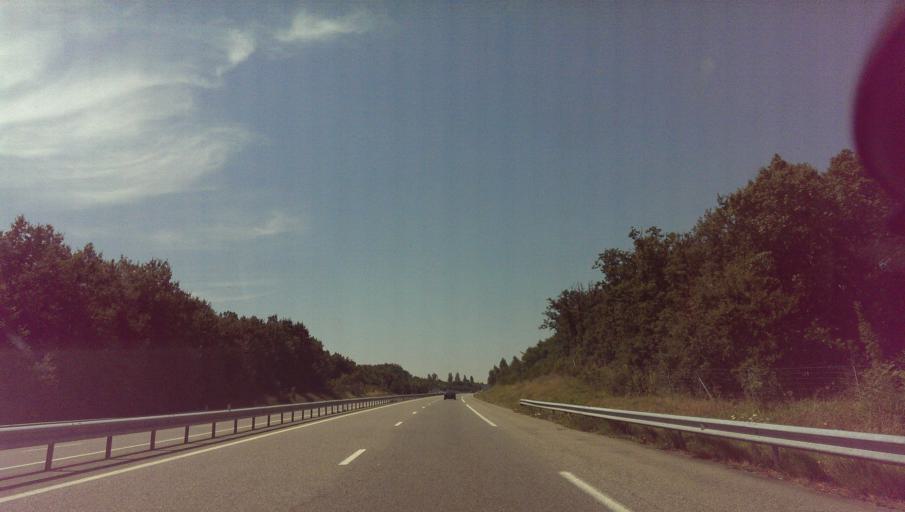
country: FR
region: Midi-Pyrenees
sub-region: Departement de la Haute-Garonne
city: Nailloux
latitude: 43.3964
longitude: 1.6374
